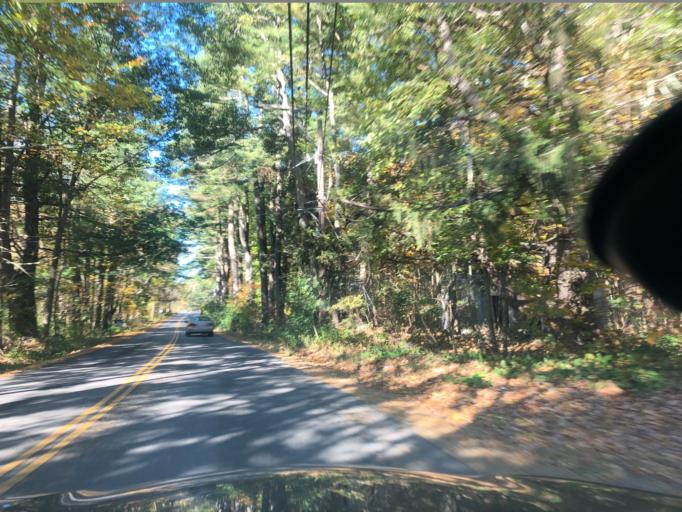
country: US
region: New Hampshire
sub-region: Rockingham County
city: Newmarket
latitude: 43.1120
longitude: -70.9610
